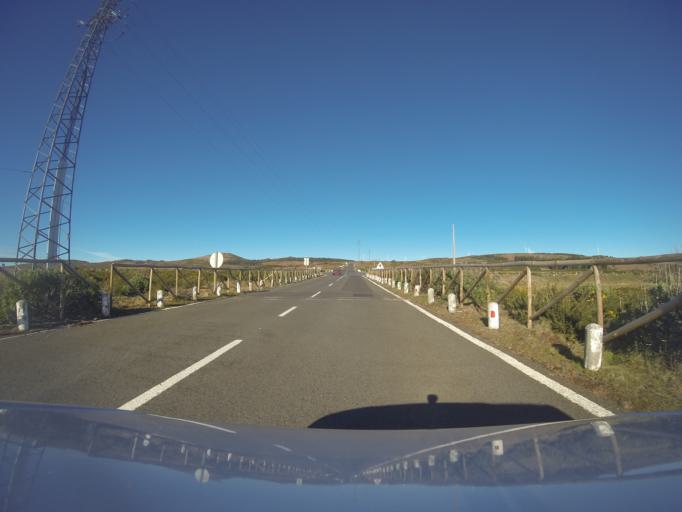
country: PT
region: Madeira
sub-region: Sao Vicente
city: Sao Vicente
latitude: 32.7590
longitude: -17.0944
